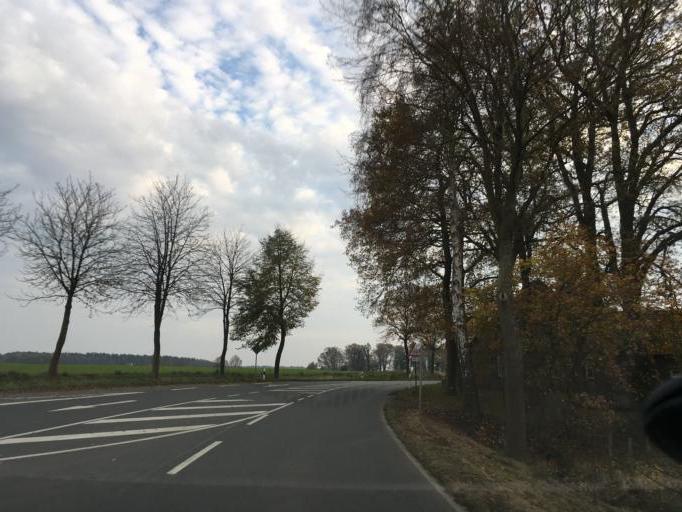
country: DE
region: Lower Saxony
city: Wietzendorf
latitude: 52.9104
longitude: 9.9840
